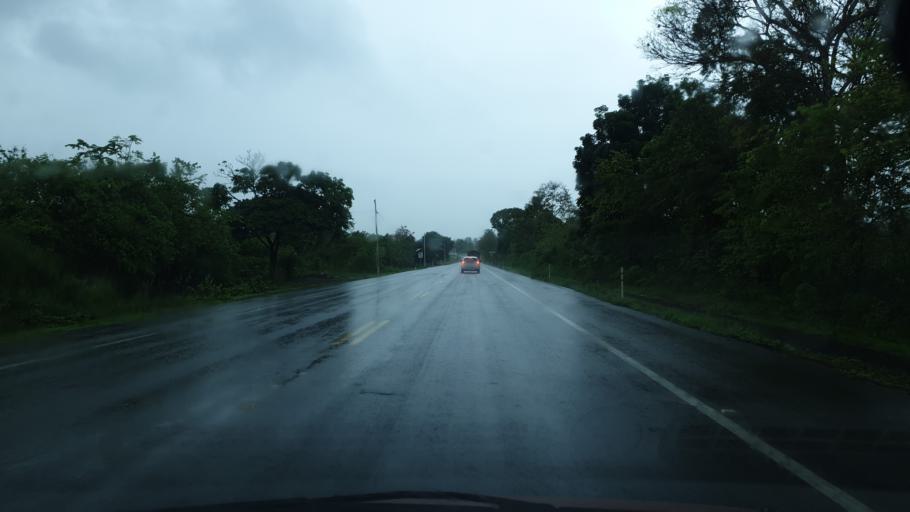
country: EC
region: Manabi
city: Pajan
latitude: -1.7060
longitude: -80.4205
